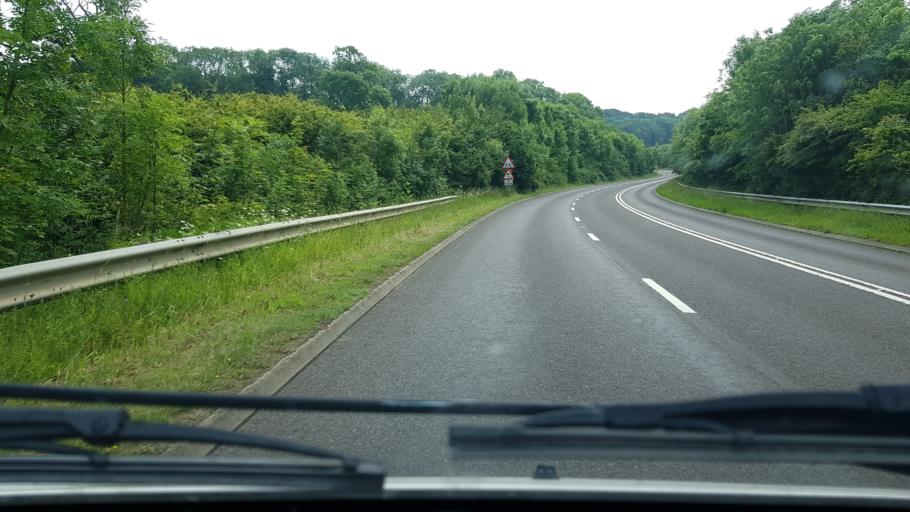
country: GB
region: England
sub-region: Worcestershire
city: Broadway
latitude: 52.0362
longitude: -1.8421
